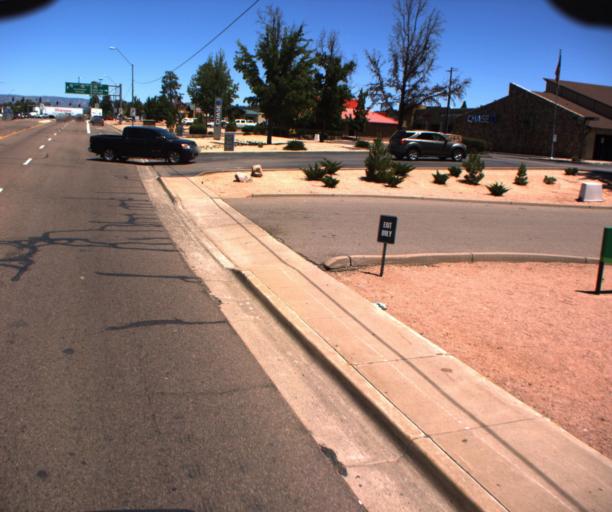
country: US
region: Arizona
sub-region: Gila County
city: Payson
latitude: 34.2386
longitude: -111.3230
